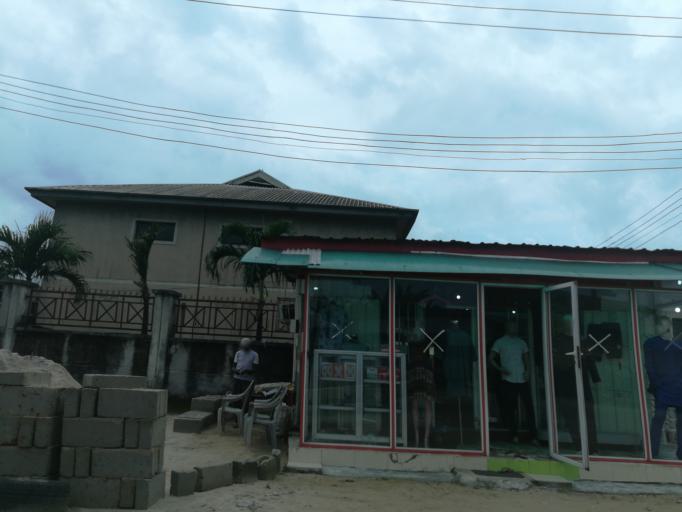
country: NG
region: Rivers
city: Port Harcourt
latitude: 4.7650
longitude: 7.0251
